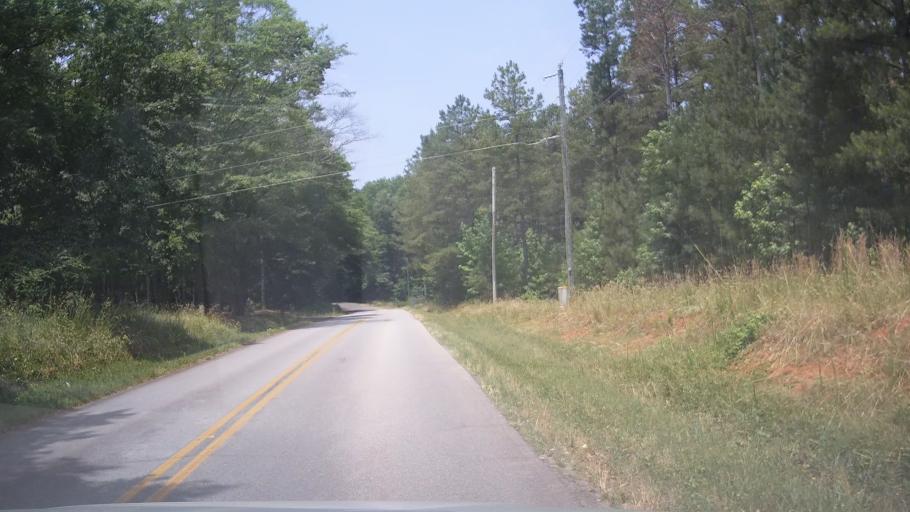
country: US
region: Georgia
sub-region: Hart County
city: Hartwell
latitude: 34.3471
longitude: -82.9058
